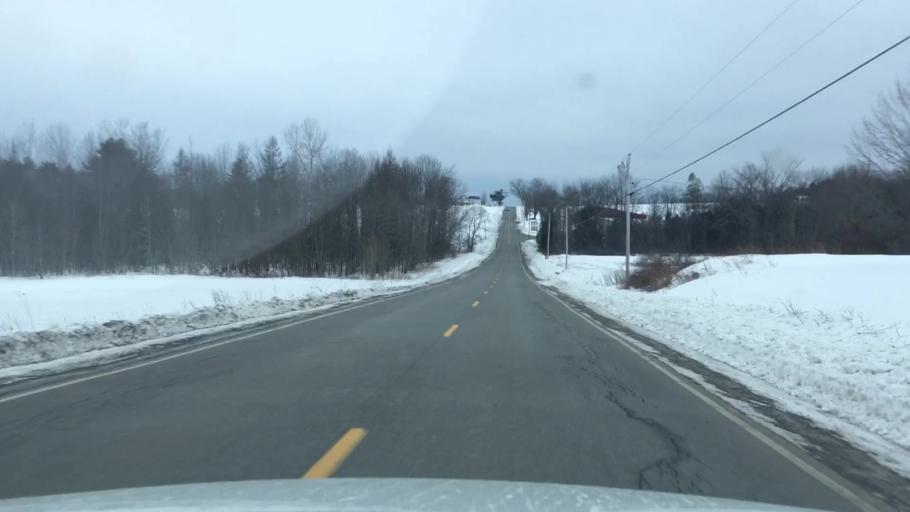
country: US
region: Maine
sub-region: Penobscot County
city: Garland
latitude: 44.9680
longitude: -69.1576
